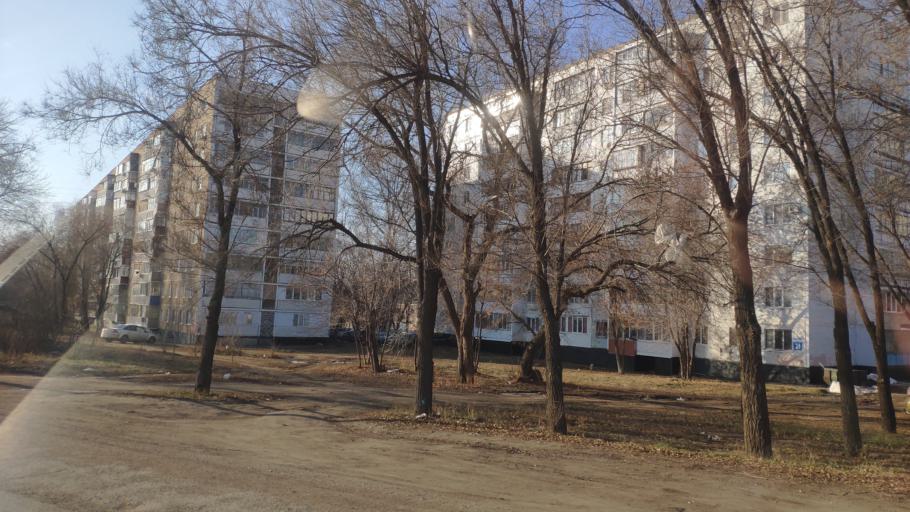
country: RU
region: Orenburg
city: Prigorodnyy
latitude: 51.7801
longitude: 55.1889
